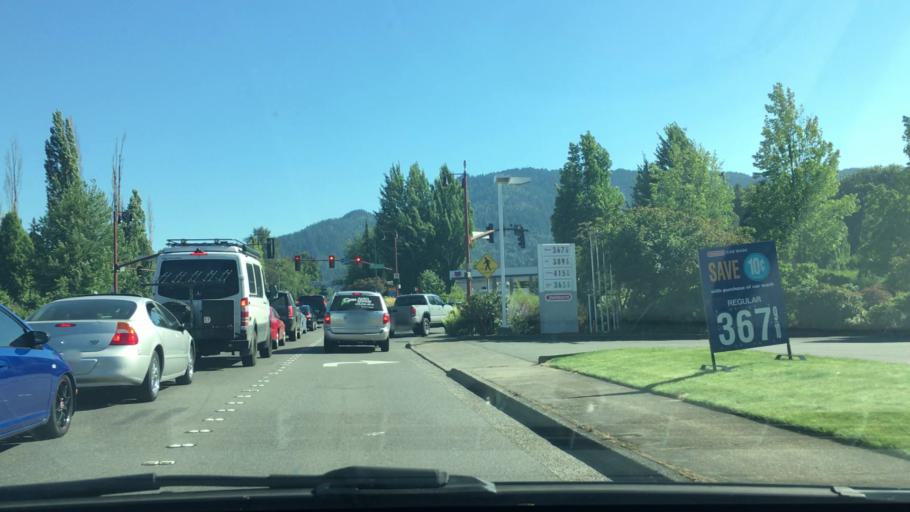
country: US
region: Washington
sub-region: King County
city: Issaquah
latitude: 47.5388
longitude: -122.0364
